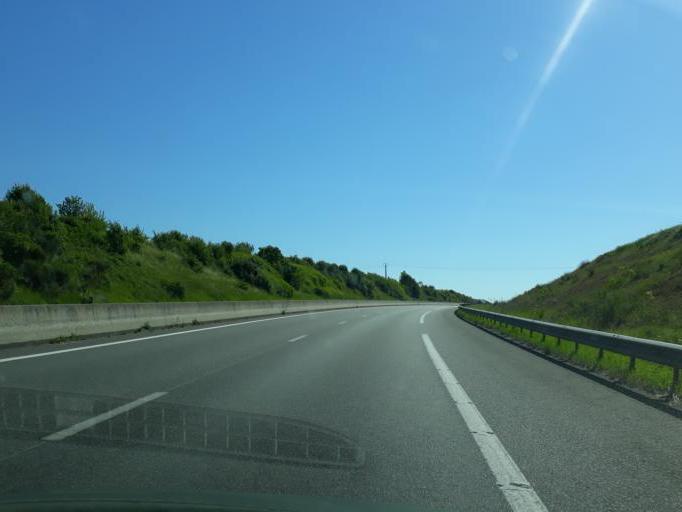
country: FR
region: Centre
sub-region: Departement du Loiret
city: Courtenay
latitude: 48.0443
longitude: 3.0410
